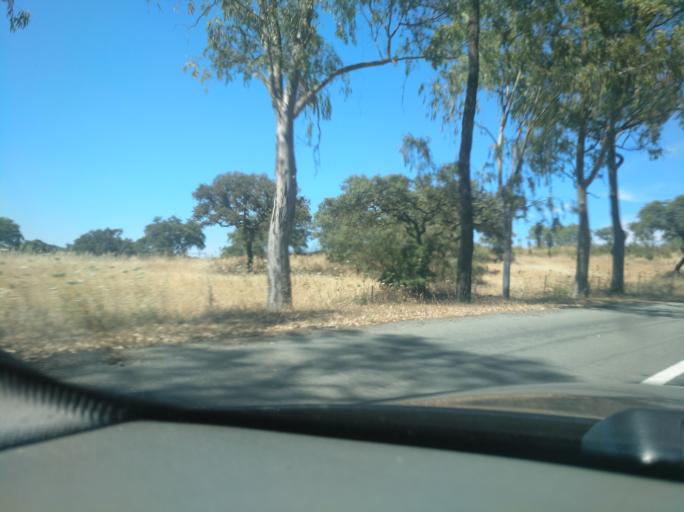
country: PT
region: Beja
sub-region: Almodovar
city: Almodovar
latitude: 37.5412
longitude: -7.9876
